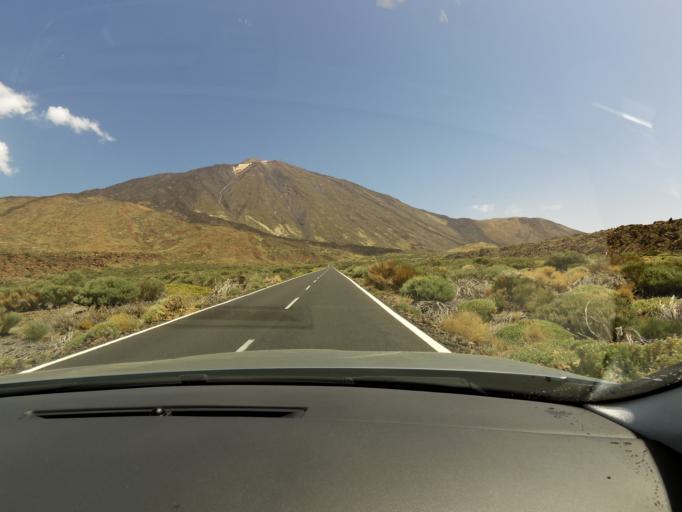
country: ES
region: Canary Islands
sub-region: Provincia de Santa Cruz de Tenerife
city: Vilaflor
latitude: 28.2349
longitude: -16.6295
